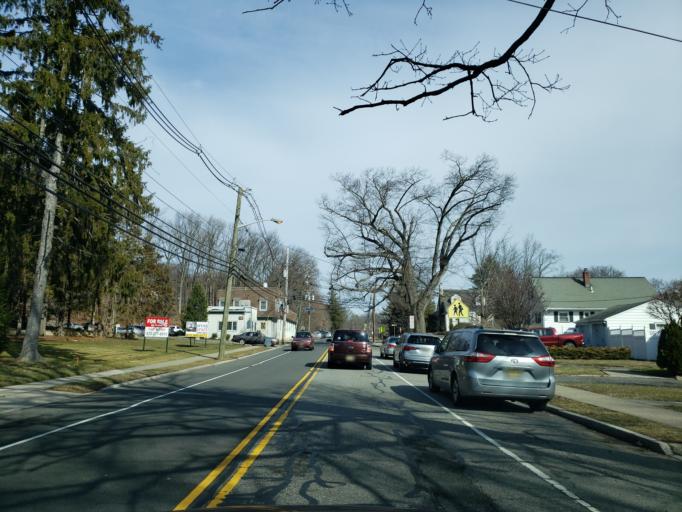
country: US
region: New Jersey
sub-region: Essex County
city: Verona
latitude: 40.8392
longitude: -74.2495
